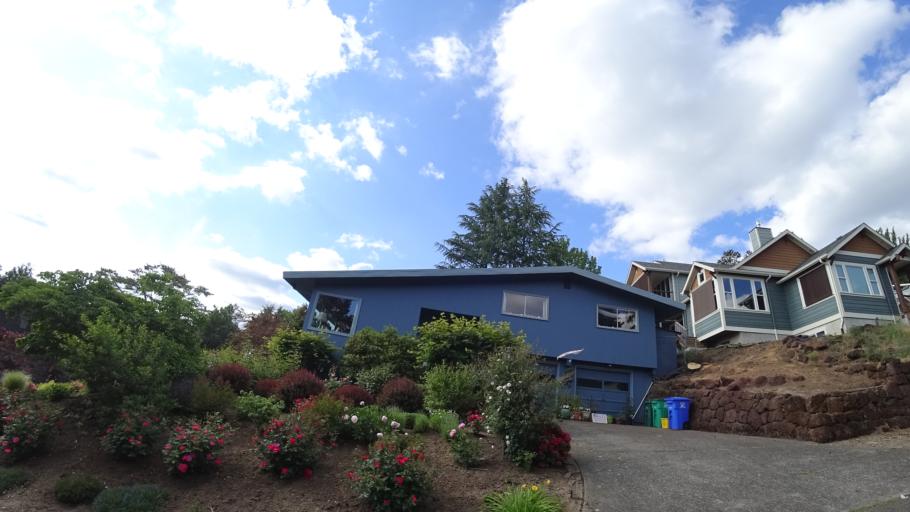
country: US
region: Oregon
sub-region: Washington County
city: Garden Home-Whitford
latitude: 45.4780
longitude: -122.7196
